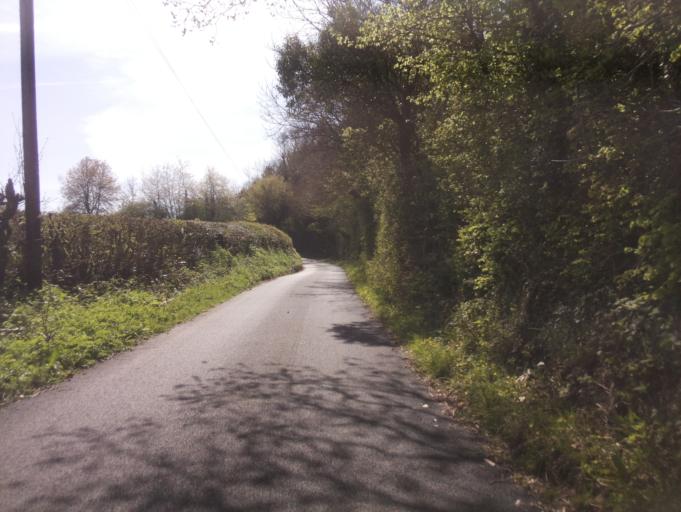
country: GB
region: Wales
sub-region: Monmouthshire
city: Llangwm
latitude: 51.7485
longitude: -2.8306
